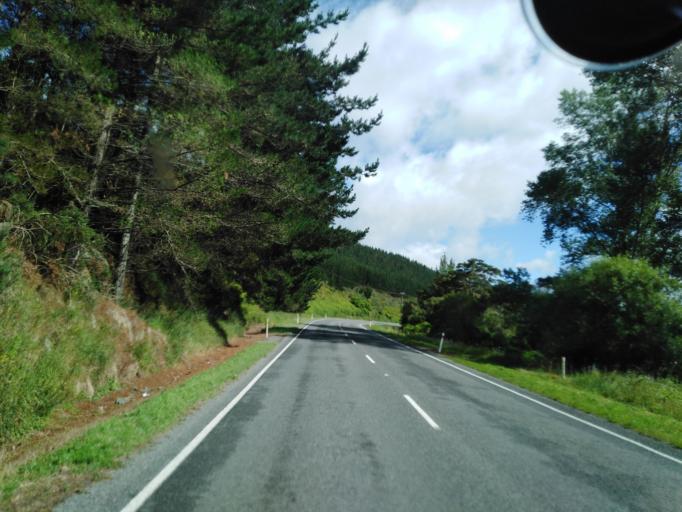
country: NZ
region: Nelson
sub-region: Nelson City
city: Nelson
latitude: -41.2475
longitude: 173.5774
